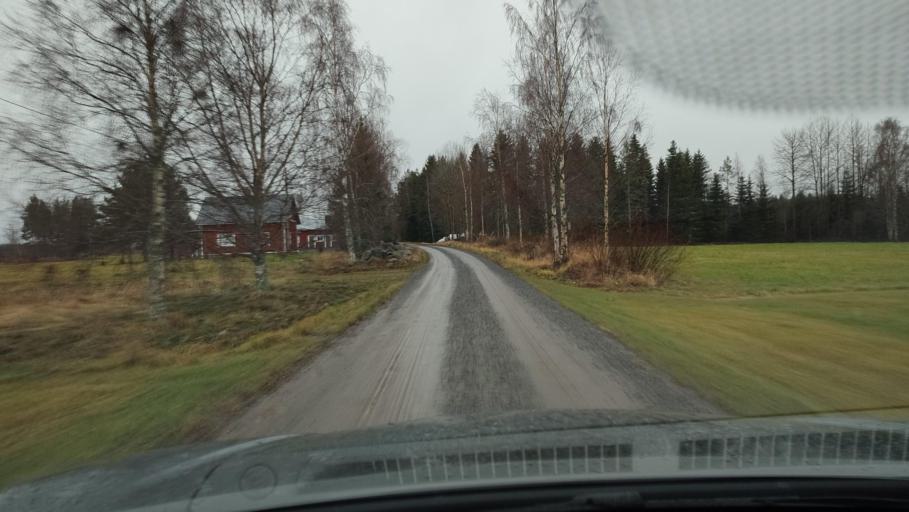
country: FI
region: Southern Ostrobothnia
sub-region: Suupohja
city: Karijoki
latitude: 62.2372
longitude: 21.5501
